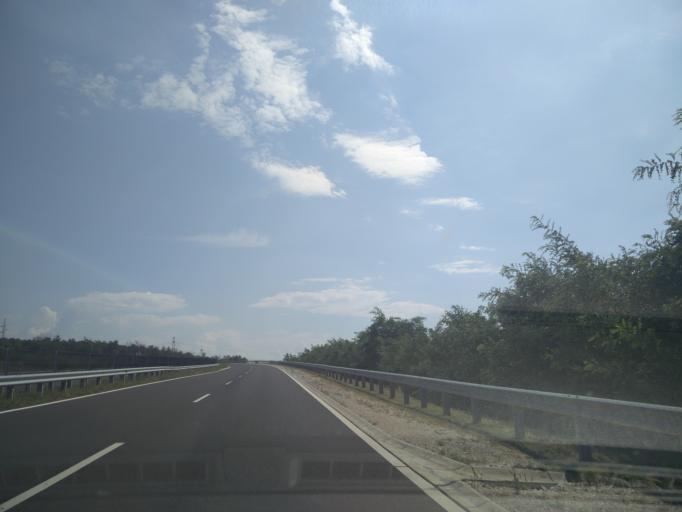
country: HU
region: Zala
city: Heviz
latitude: 46.7911
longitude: 17.1307
